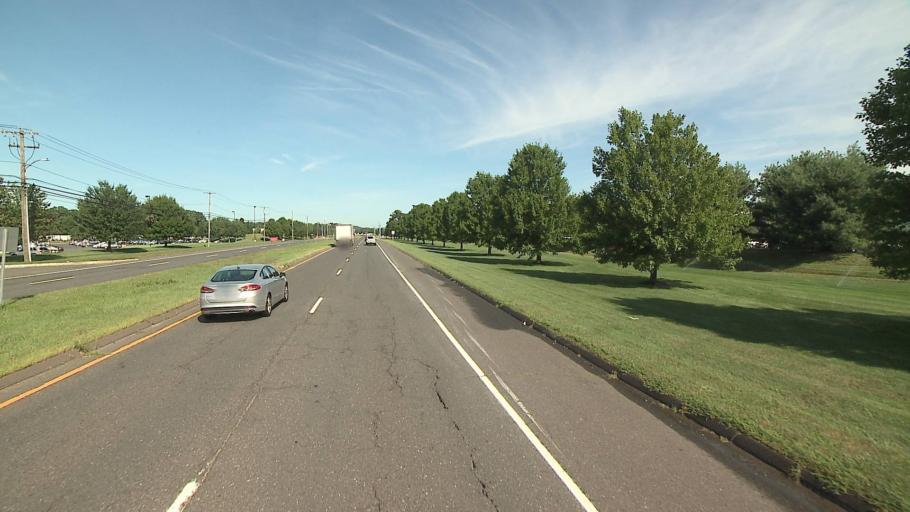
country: US
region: Connecticut
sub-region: Hartford County
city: Tariffville
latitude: 41.8671
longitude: -72.7195
